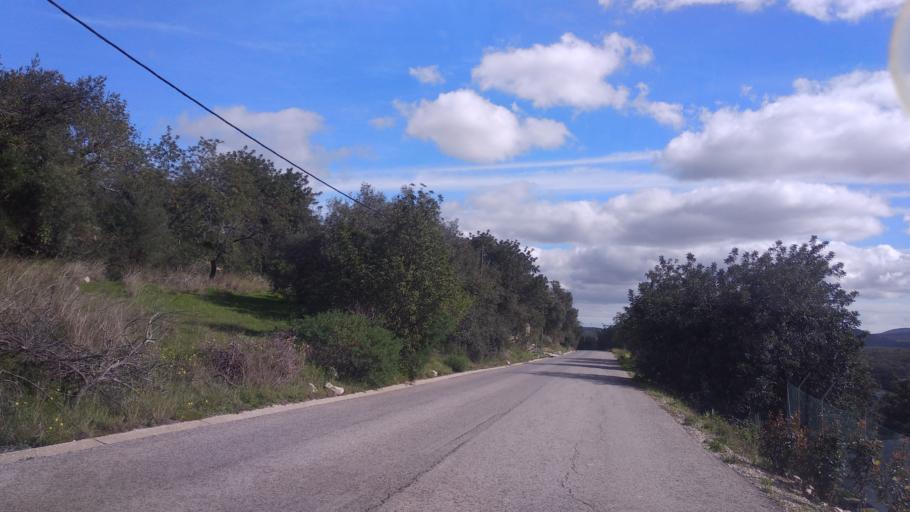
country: PT
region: Faro
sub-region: Sao Bras de Alportel
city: Sao Bras de Alportel
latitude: 37.1492
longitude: -7.9114
